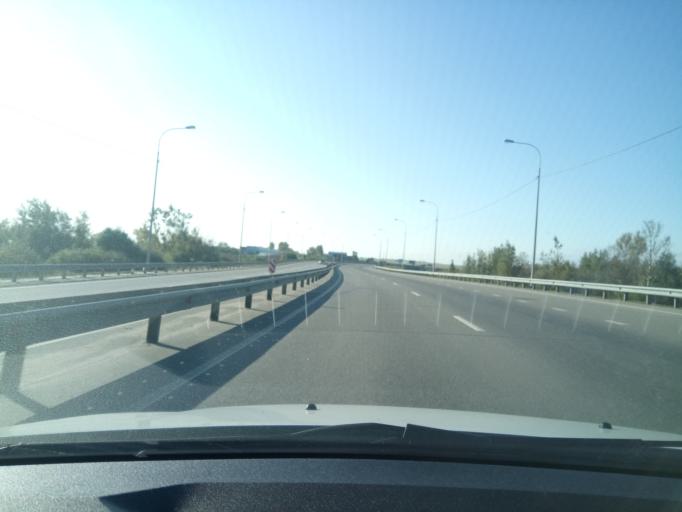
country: RU
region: Nizjnij Novgorod
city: Burevestnik
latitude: 56.1587
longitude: 43.9114
